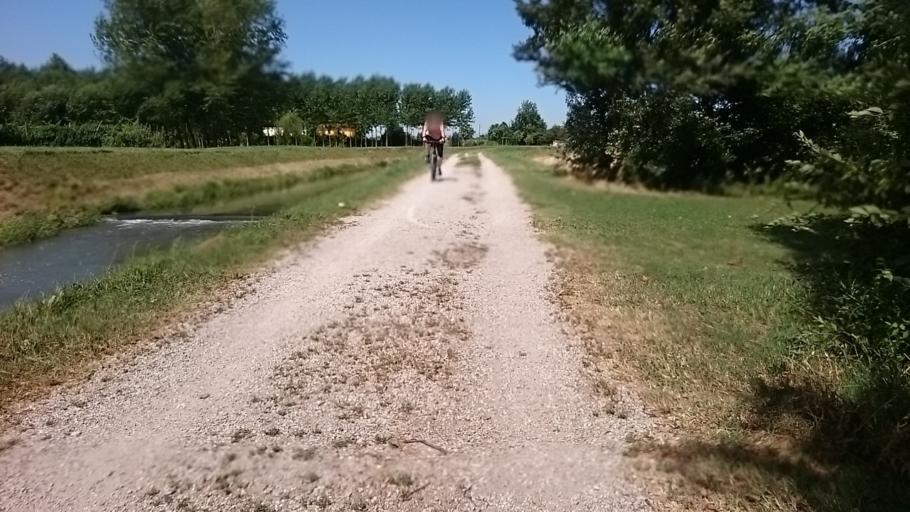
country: IT
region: Veneto
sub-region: Provincia di Padova
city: Pionca
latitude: 45.4692
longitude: 11.9538
